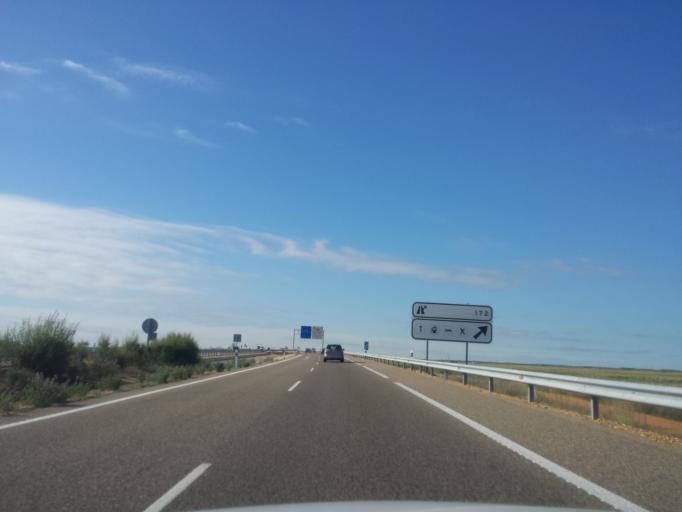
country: ES
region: Castille and Leon
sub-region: Provincia de Leon
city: Villamanan
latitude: 42.3341
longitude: -5.6094
